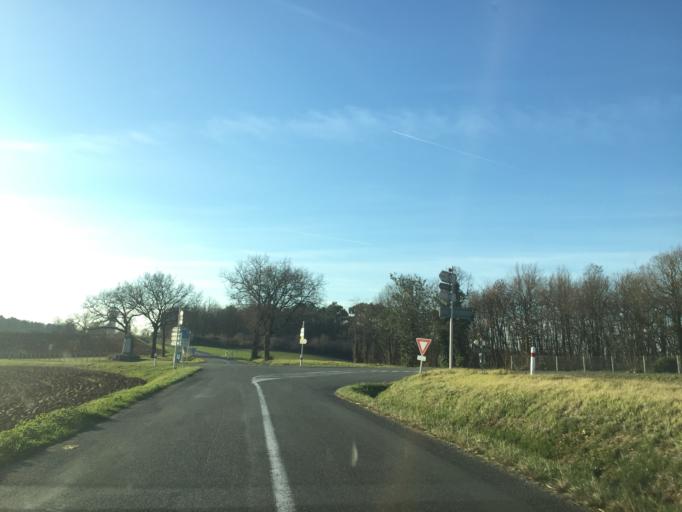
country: FR
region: Aquitaine
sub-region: Departement de la Dordogne
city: Riberac
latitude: 45.2240
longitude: 0.2906
